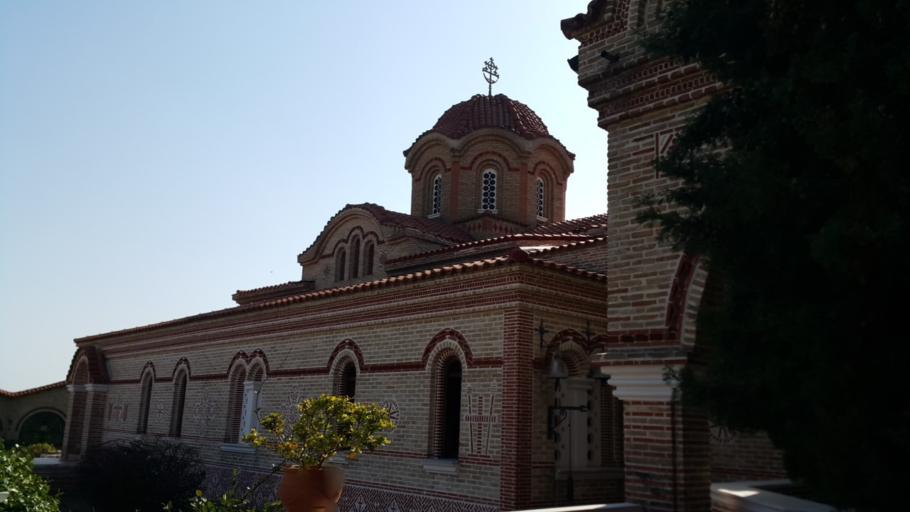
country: GR
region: Central Macedonia
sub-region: Nomos Pierias
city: Kontariotissa
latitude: 40.2383
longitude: 22.4515
